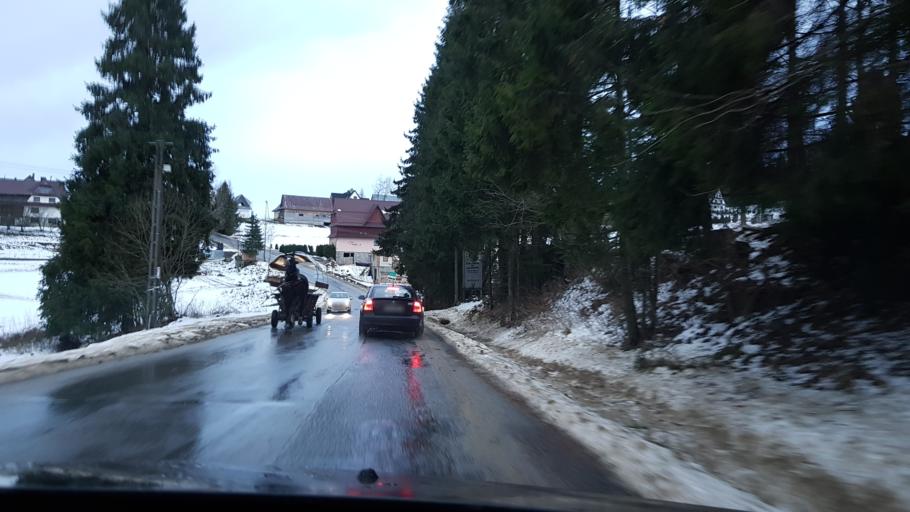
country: PL
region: Lesser Poland Voivodeship
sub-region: Powiat tatrzanski
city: Bukowina Tatrzanska
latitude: 49.3183
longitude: 20.1136
